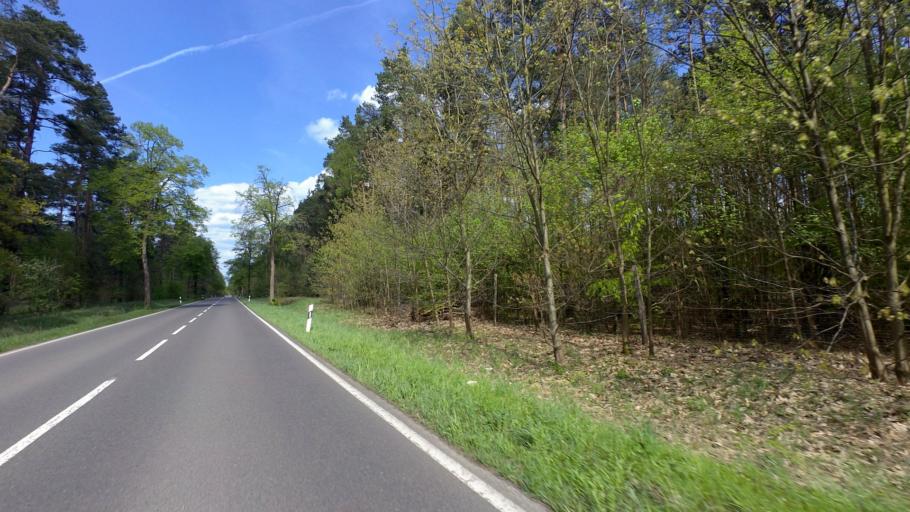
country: DE
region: Brandenburg
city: Milmersdorf
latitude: 53.0819
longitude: 13.6226
